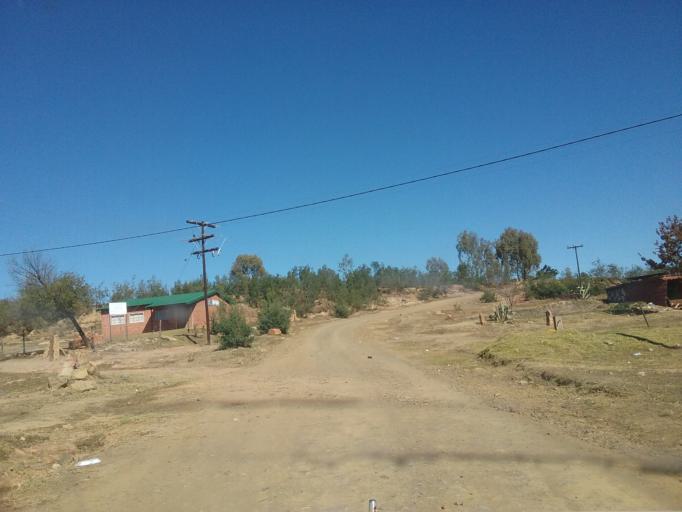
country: LS
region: Maseru
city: Maseru
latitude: -29.4491
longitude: 27.5793
